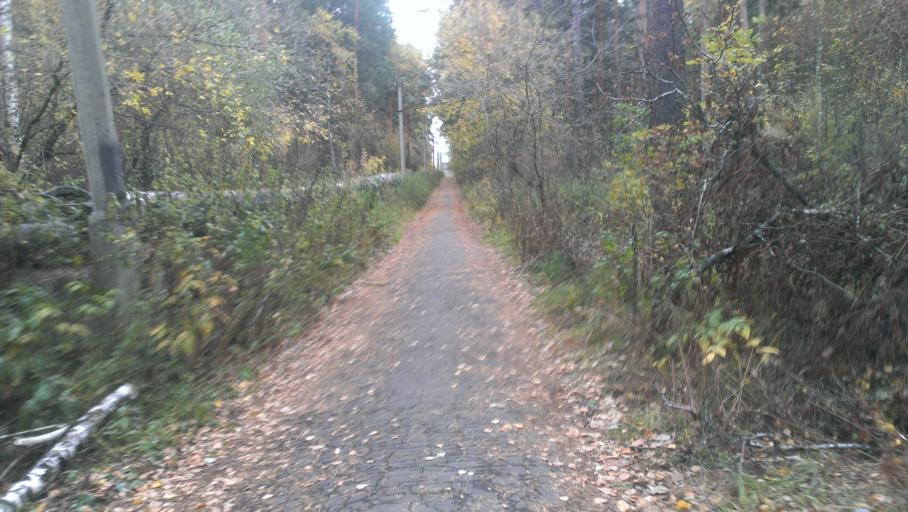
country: RU
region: Altai Krai
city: Yuzhnyy
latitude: 53.2608
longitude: 83.6881
